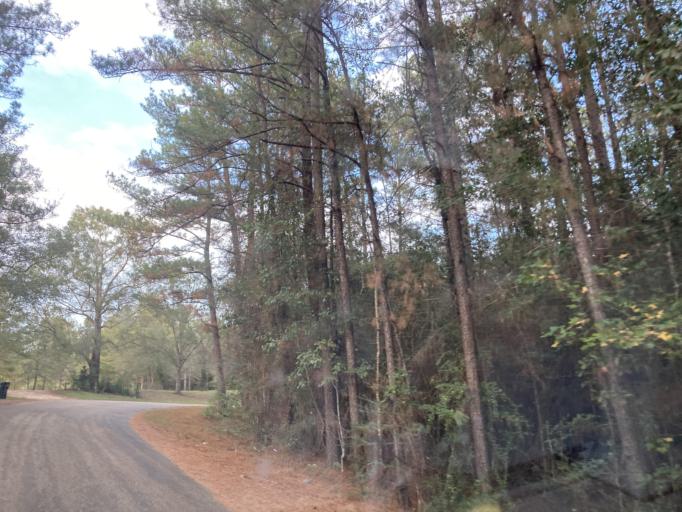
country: US
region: Mississippi
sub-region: Lamar County
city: Purvis
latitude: 31.2036
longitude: -89.3589
